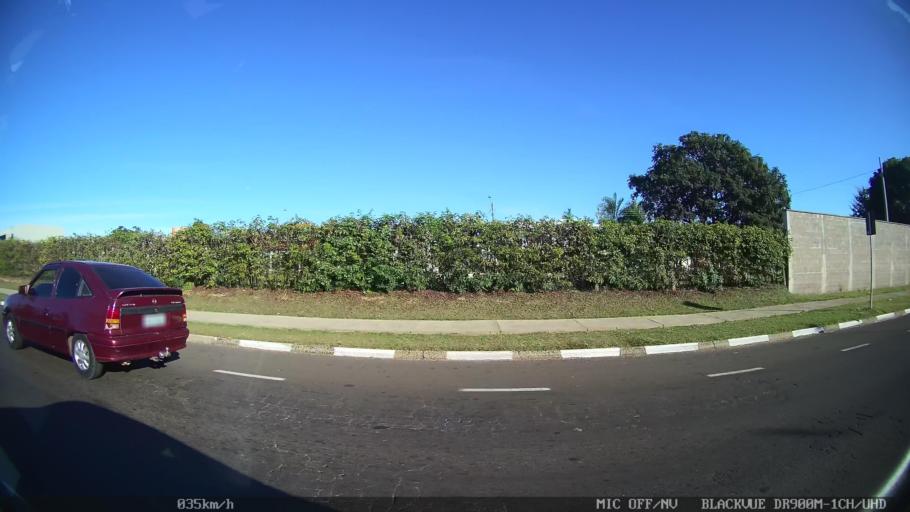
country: BR
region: Sao Paulo
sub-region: Franca
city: Franca
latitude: -20.5643
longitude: -47.3648
